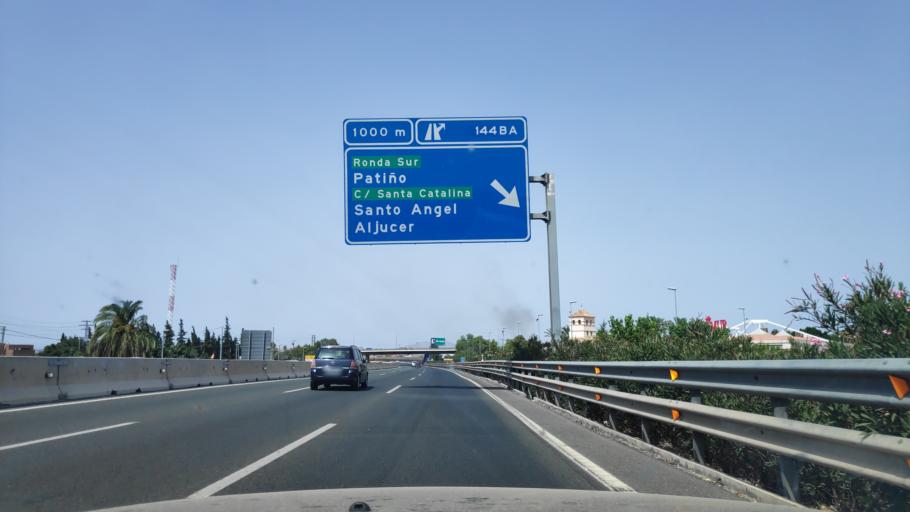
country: ES
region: Murcia
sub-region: Murcia
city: Murcia
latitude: 37.9554
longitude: -1.1381
